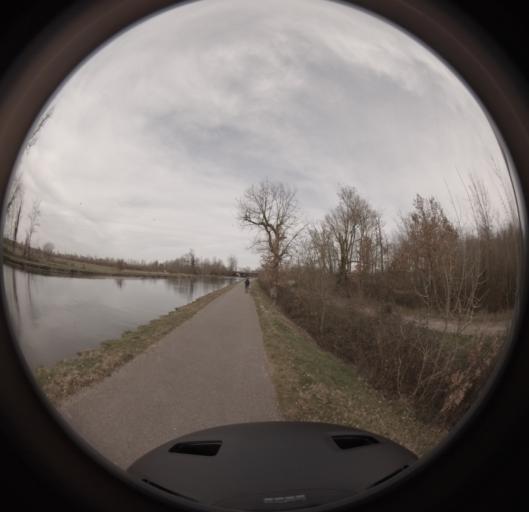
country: FR
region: Midi-Pyrenees
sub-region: Departement du Tarn-et-Garonne
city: Montech
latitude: 43.9796
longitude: 1.2512
